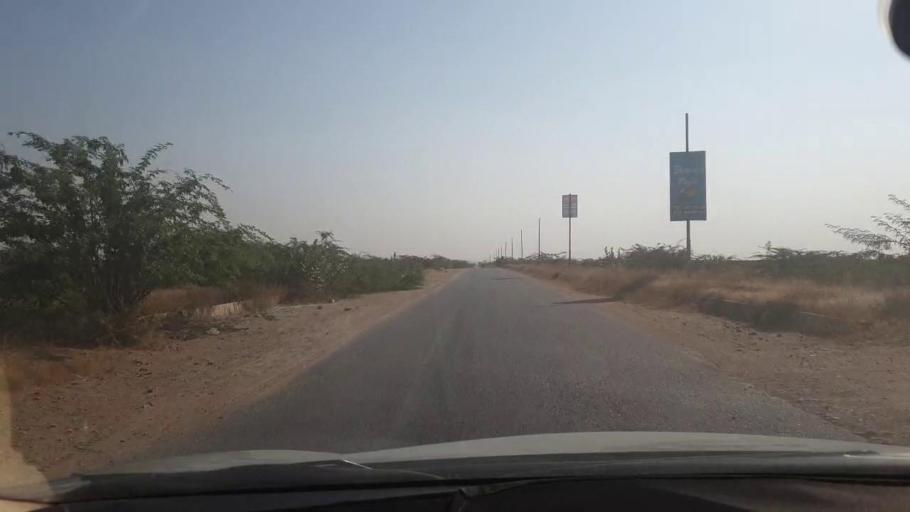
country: PK
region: Sindh
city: Malir Cantonment
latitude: 25.0685
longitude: 67.1388
